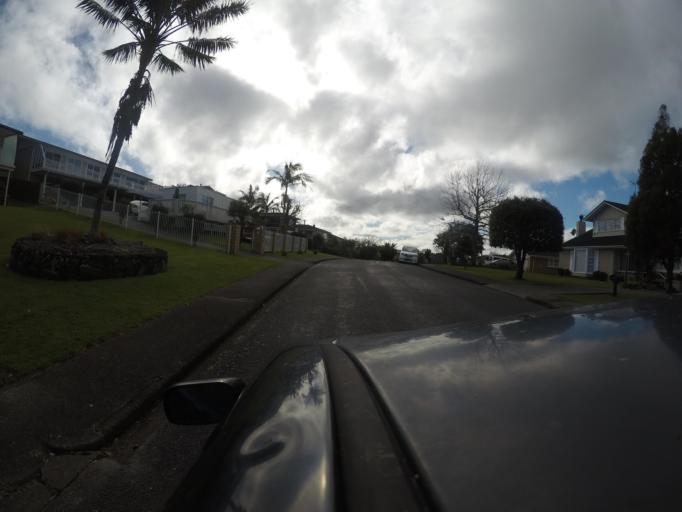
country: NZ
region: Auckland
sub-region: Auckland
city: Waitakere
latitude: -36.8914
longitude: 174.6462
